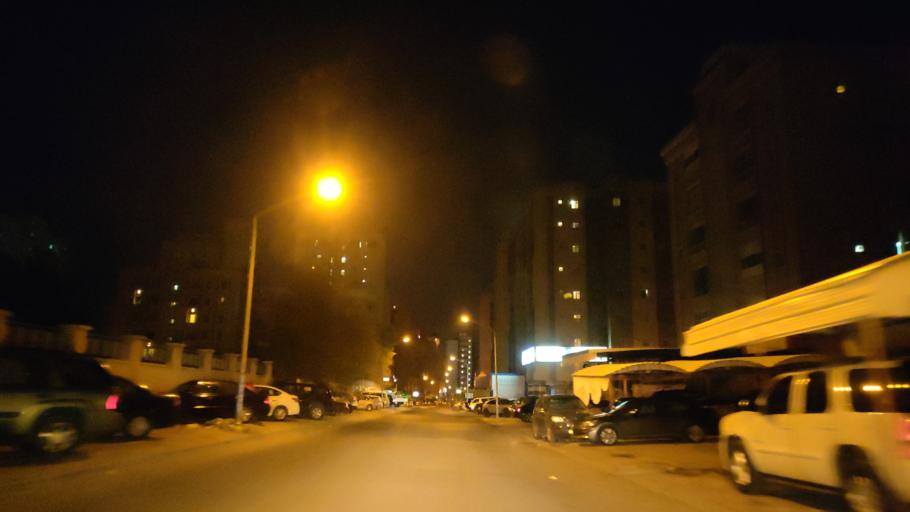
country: KW
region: Muhafazat Hawalli
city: Hawalli
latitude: 29.3278
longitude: 48.0514
